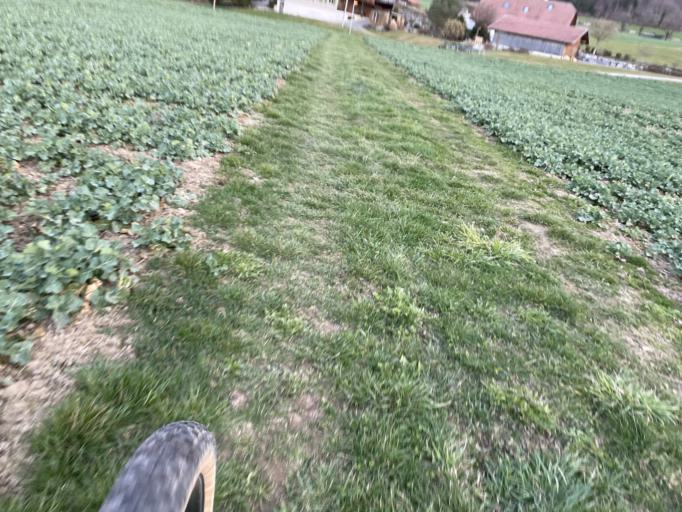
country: CH
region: Bern
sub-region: Bern-Mittelland District
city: Niederwichtrach
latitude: 46.8446
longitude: 7.5846
